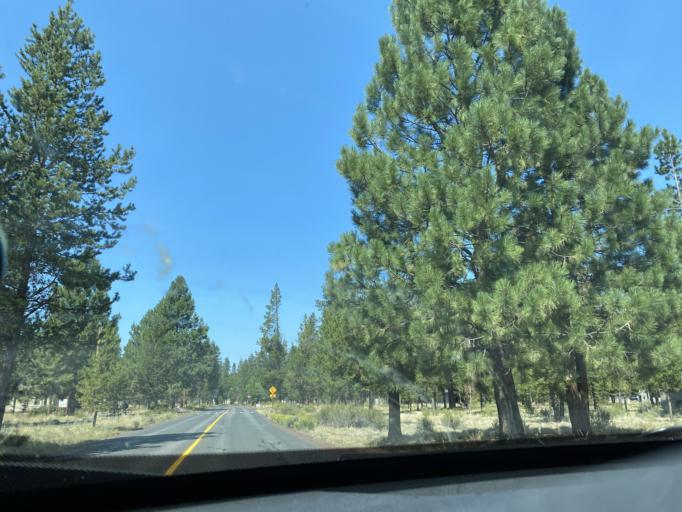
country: US
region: Oregon
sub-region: Deschutes County
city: Sunriver
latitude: 43.8927
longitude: -121.4204
